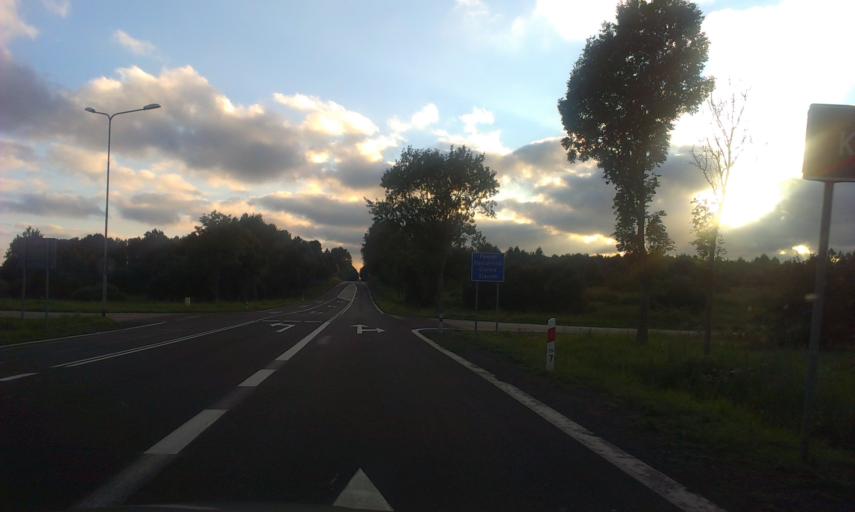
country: PL
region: West Pomeranian Voivodeship
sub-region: Powiat koszalinski
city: Sianow
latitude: 54.2603
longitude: 16.4011
